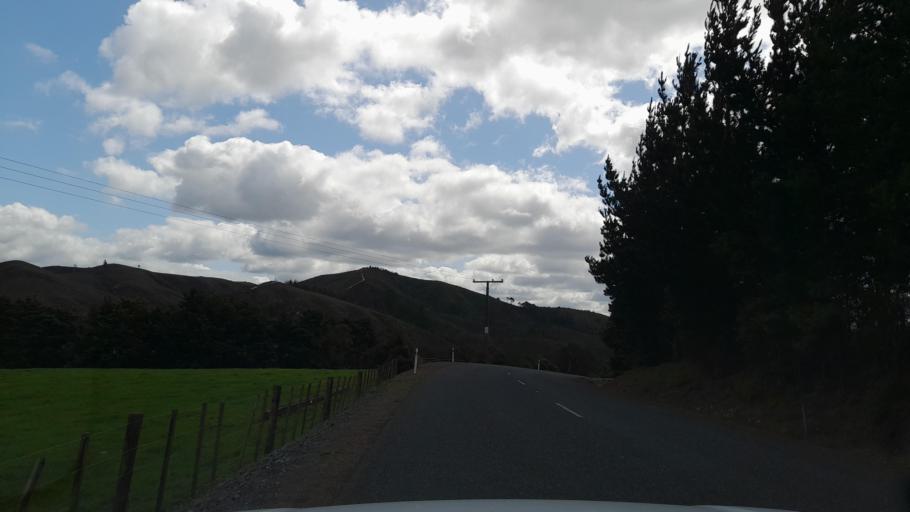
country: NZ
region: Northland
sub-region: Whangarei
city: Maungatapere
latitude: -35.6854
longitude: 174.0412
